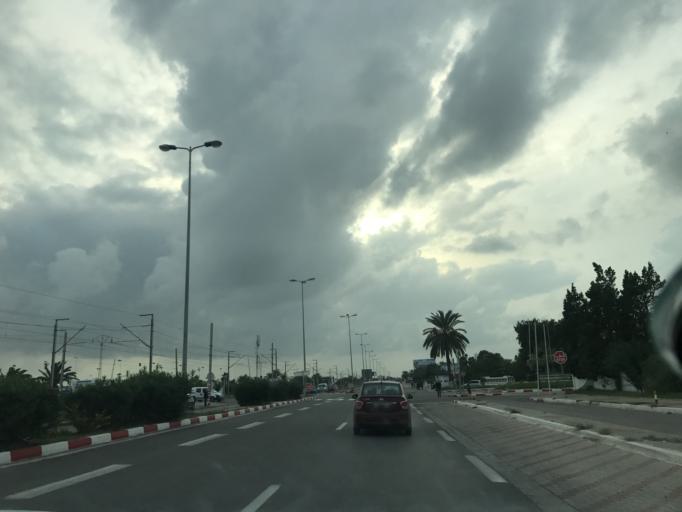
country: TN
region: Al Munastir
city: Sahline
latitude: 35.7623
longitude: 10.7525
